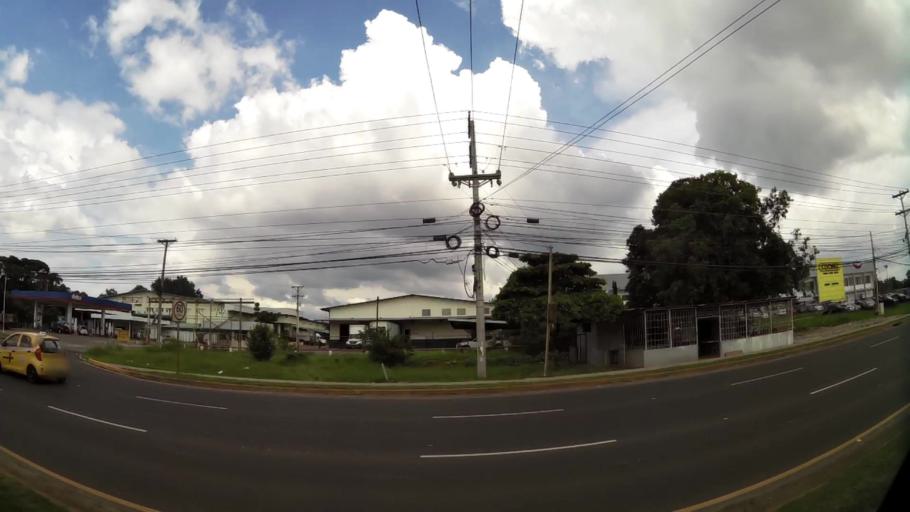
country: PA
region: Panama
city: Tocumen
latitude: 9.0683
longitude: -79.4088
